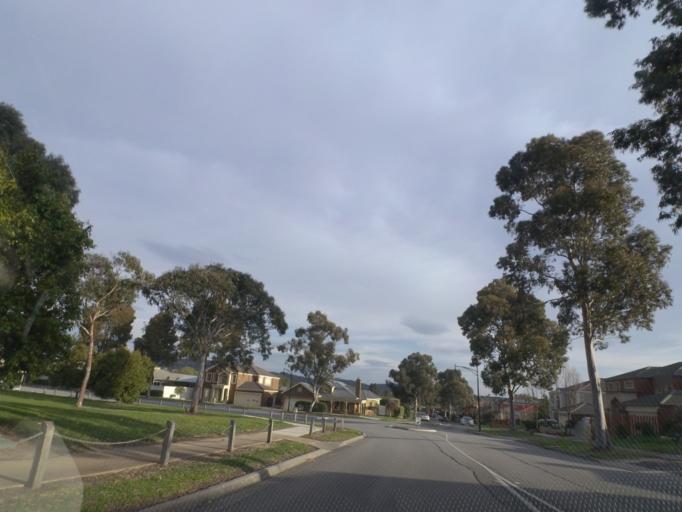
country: AU
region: Victoria
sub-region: Knox
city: Knoxfield
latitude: -37.9063
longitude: 145.2691
